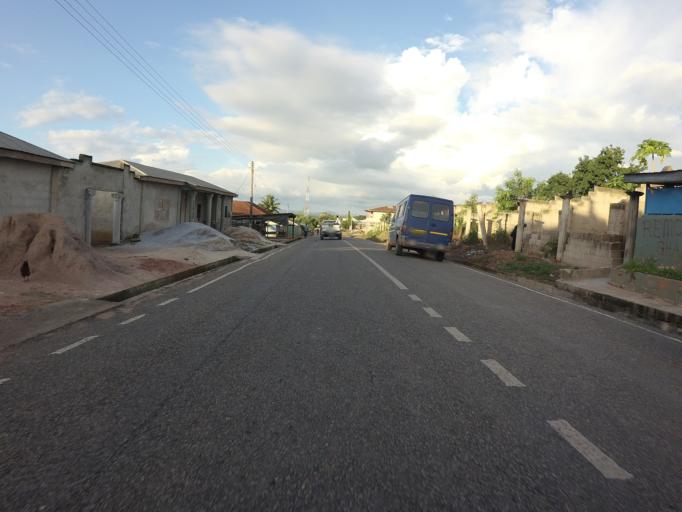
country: GH
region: Ashanti
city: Tafo
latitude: 6.9408
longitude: -1.6778
